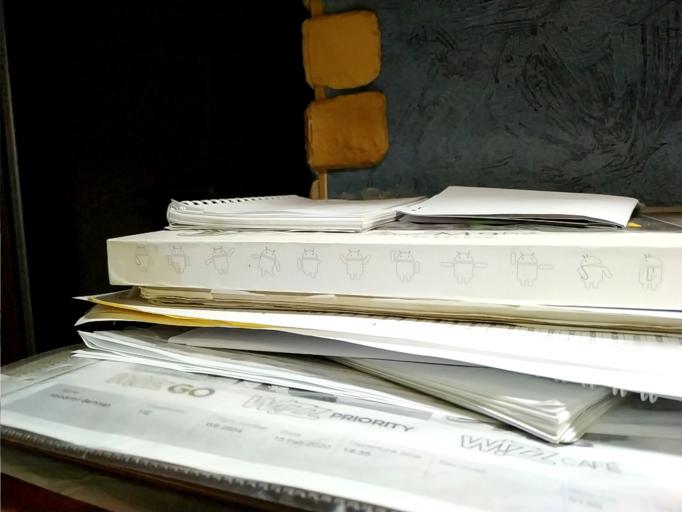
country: RU
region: Arkhangelskaya
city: Onega
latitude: 63.4858
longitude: 38.1540
